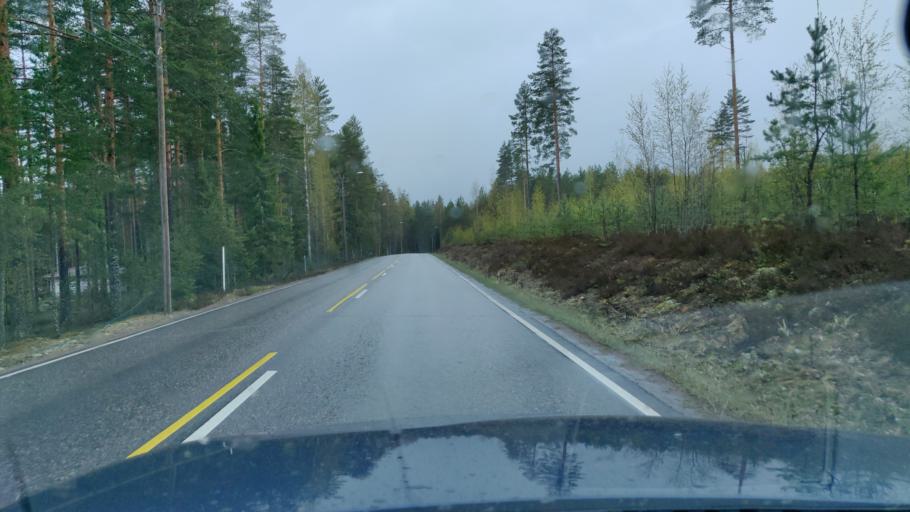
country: FI
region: Uusimaa
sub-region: Helsinki
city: Nurmijaervi
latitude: 60.5060
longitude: 24.7016
